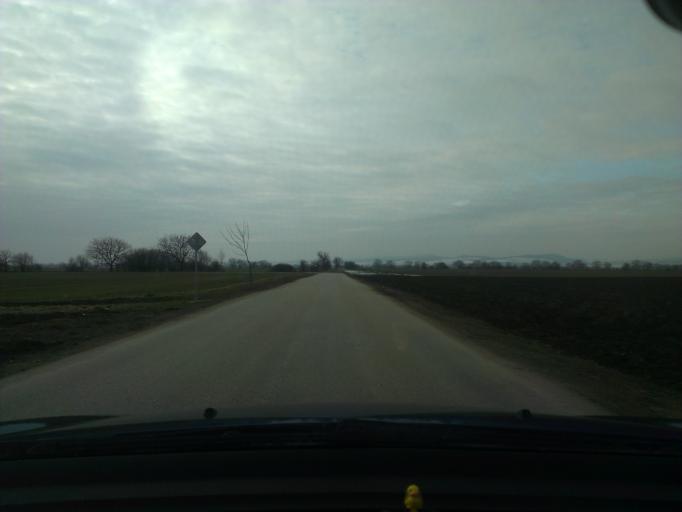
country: SK
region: Trnavsky
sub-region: Okres Trnava
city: Piestany
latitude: 48.6010
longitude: 17.8120
